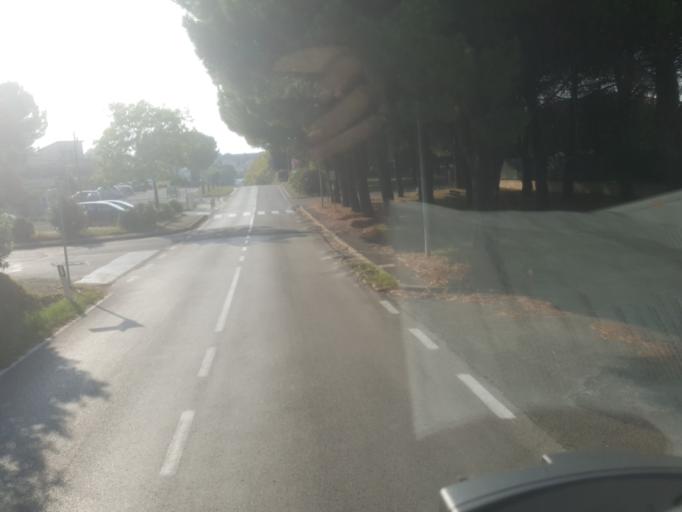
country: IT
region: Tuscany
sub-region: Province of Florence
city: Montaione
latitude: 43.5469
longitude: 10.9240
